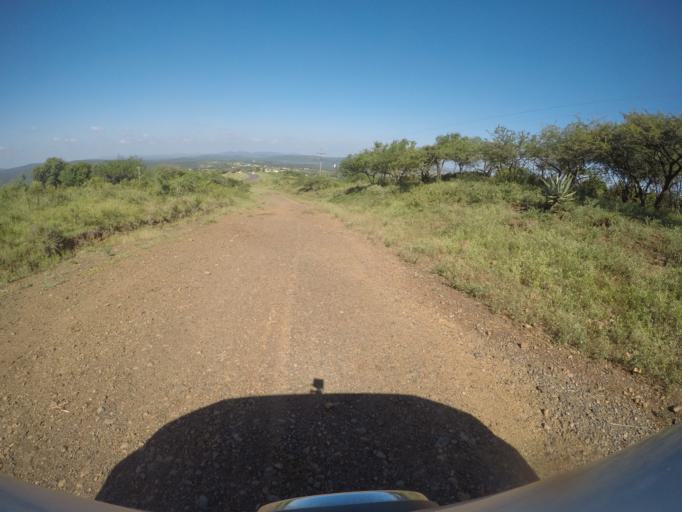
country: ZA
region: KwaZulu-Natal
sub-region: uThungulu District Municipality
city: Empangeni
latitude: -28.5708
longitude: 31.7104
